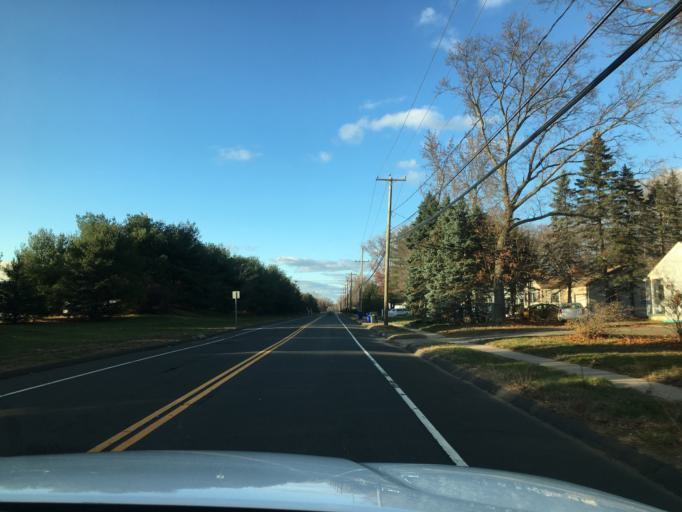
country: US
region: Connecticut
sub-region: Hartford County
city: Windsor Locks
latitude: 41.9126
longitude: -72.6586
